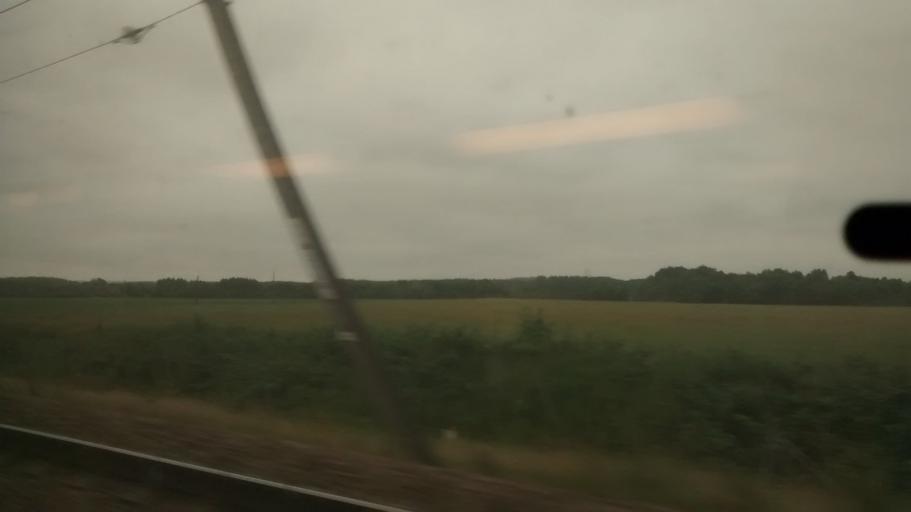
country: FR
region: Ile-de-France
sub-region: Departement de Seine-et-Marne
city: Marolles-sur-Seine
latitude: 48.3773
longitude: 3.0121
